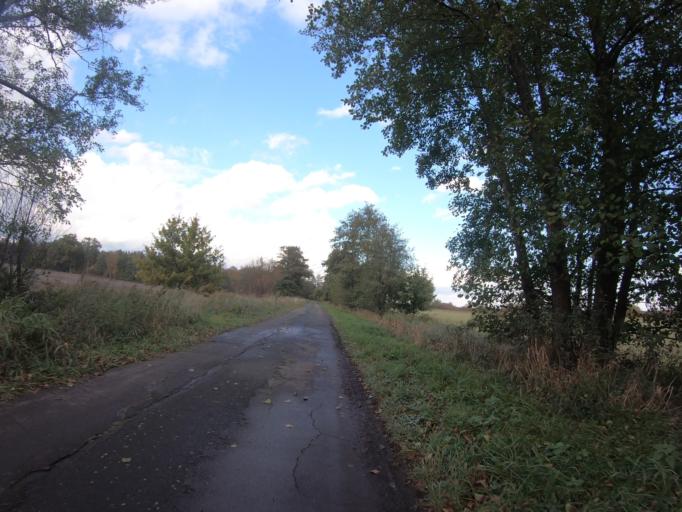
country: DE
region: Lower Saxony
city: Wagenhoff
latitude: 52.5407
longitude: 10.5545
